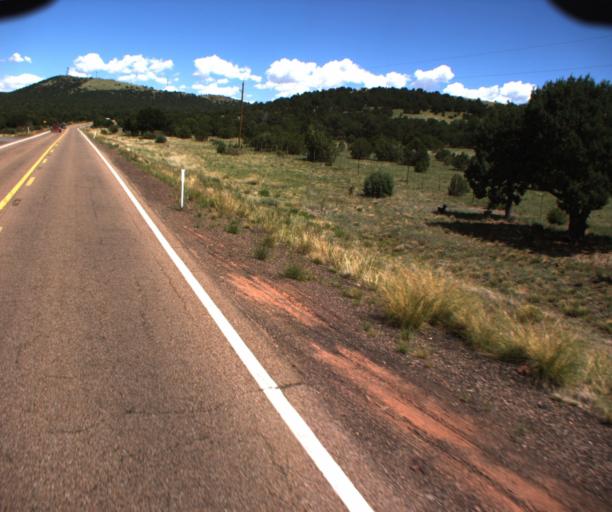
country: US
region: Arizona
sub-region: Apache County
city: Saint Johns
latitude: 34.2676
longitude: -109.6013
